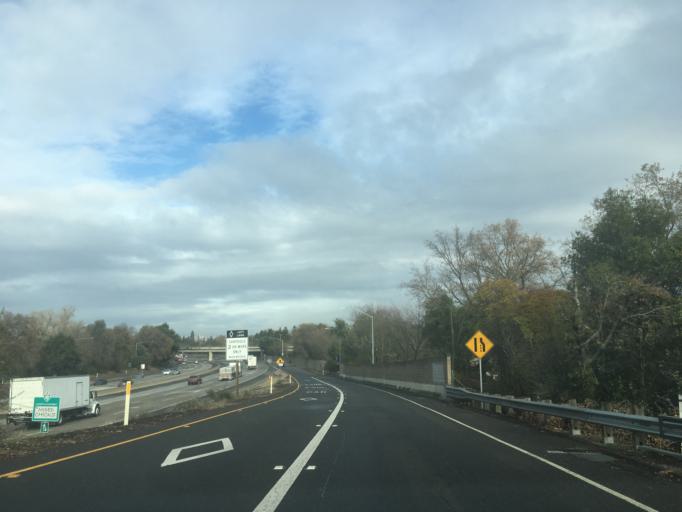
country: US
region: California
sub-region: Sacramento County
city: Sacramento
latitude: 38.5412
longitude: -121.5093
